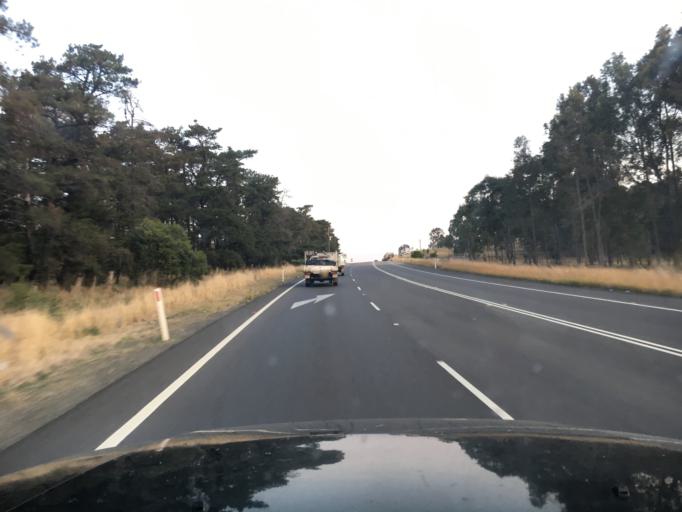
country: AU
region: New South Wales
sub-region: Cessnock
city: Greta
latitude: -32.6892
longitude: 151.4020
